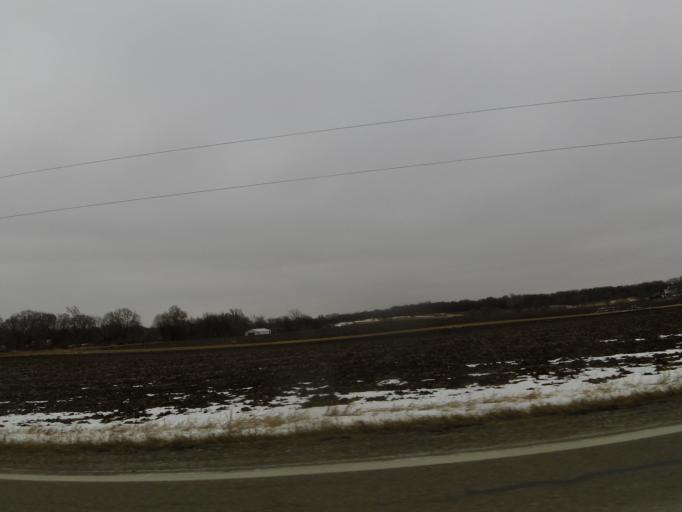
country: US
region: Minnesota
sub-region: Carver County
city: Watertown
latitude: 45.0109
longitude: -93.8487
